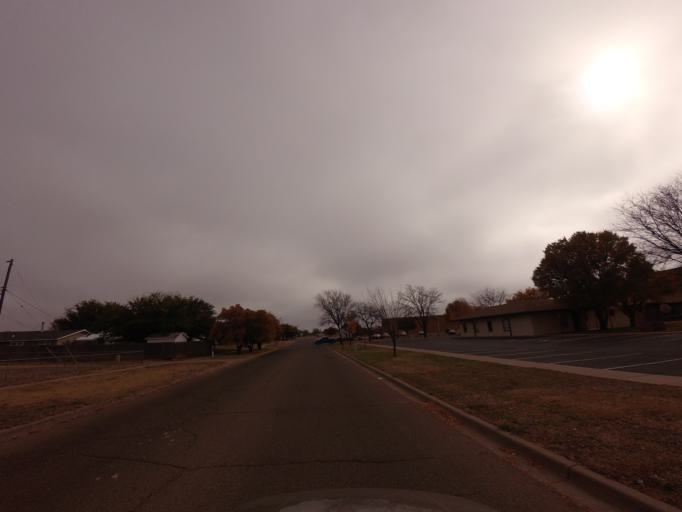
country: US
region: New Mexico
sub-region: Curry County
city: Clovis
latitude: 34.4278
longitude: -103.2272
